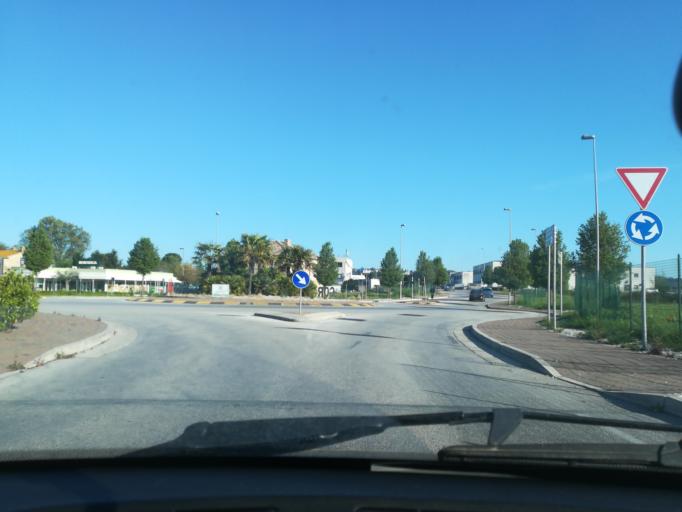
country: IT
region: The Marches
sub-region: Provincia di Macerata
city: Piediripa
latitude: 43.2692
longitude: 13.4795
